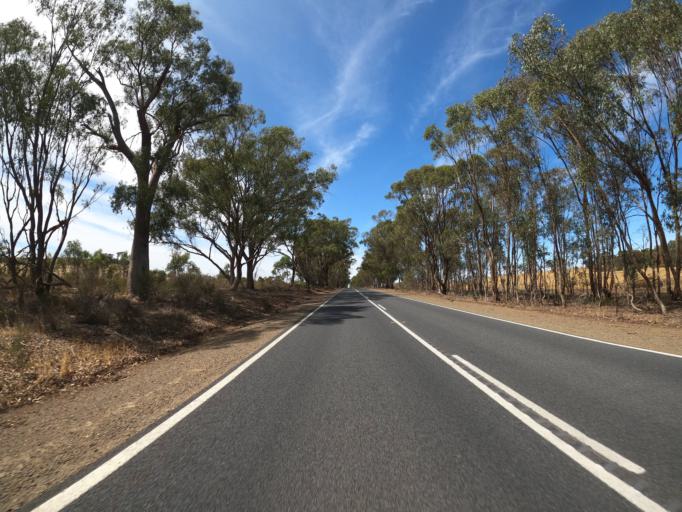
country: AU
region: Victoria
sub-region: Benalla
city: Benalla
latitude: -36.3716
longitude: 145.9728
